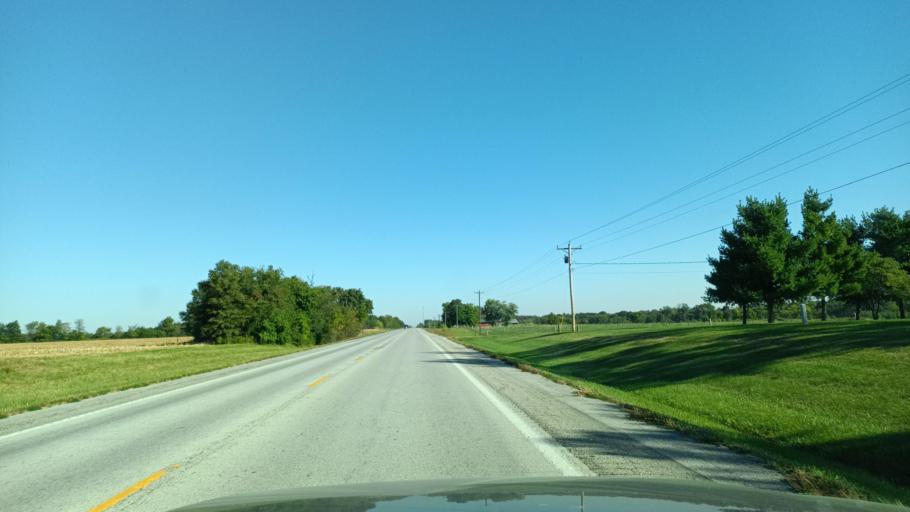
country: US
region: Missouri
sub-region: Audrain County
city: Vandalia
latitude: 39.3791
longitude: -91.6420
